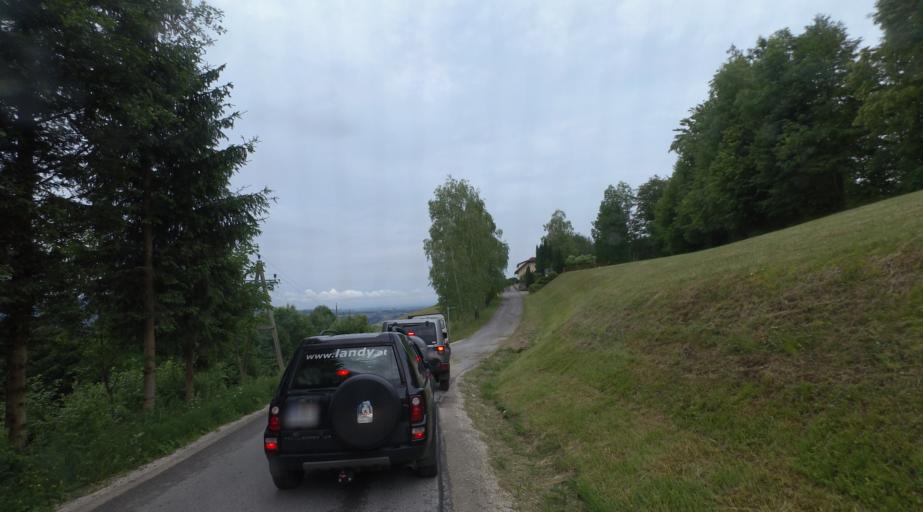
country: AT
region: Upper Austria
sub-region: Politischer Bezirk Kirchdorf an der Krems
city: Micheldorf in Oberoesterreich
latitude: 47.9374
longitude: 14.1631
